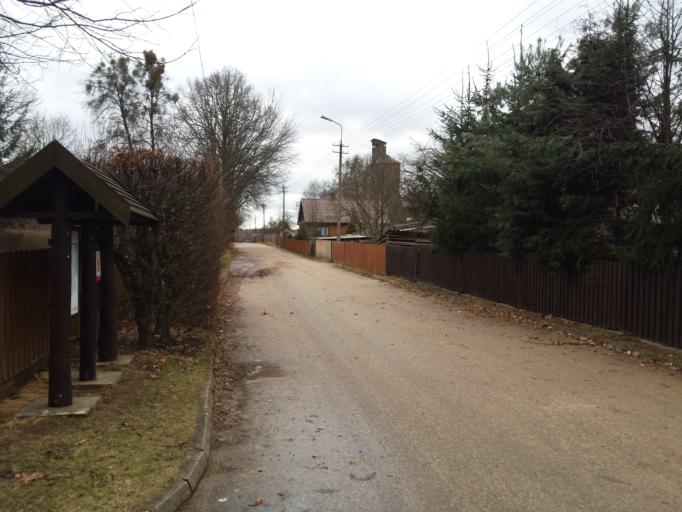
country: PL
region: Podlasie
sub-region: Powiat hajnowski
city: Bialowieza
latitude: 52.6997
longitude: 23.8838
